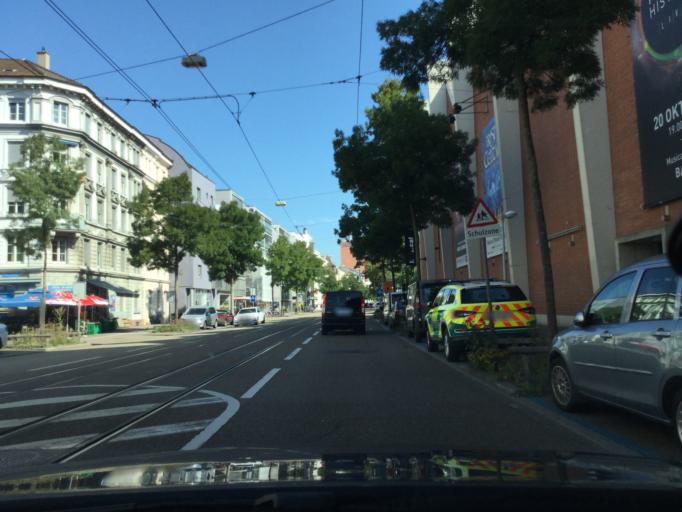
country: CH
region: Basel-City
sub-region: Basel-Stadt
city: Basel
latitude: 47.5677
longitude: 7.5975
